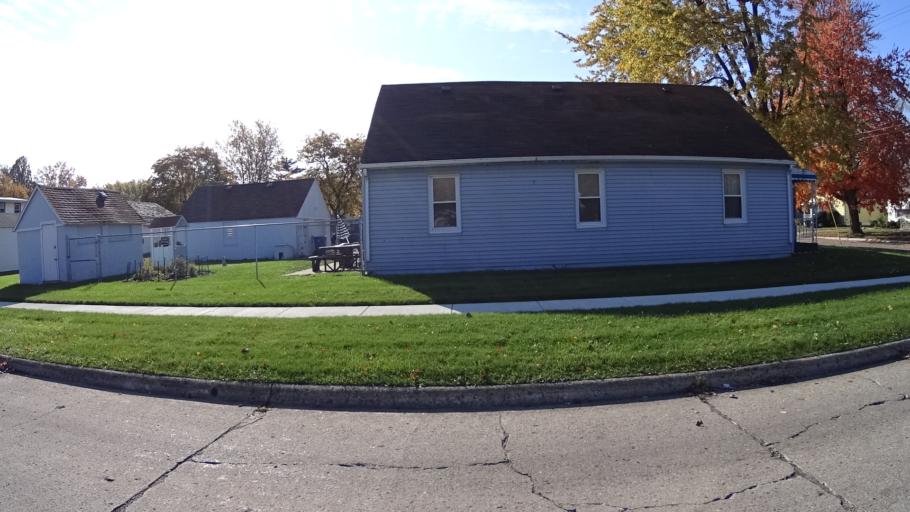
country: US
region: Ohio
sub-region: Lorain County
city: Sheffield Lake
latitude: 41.4683
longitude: -82.1383
